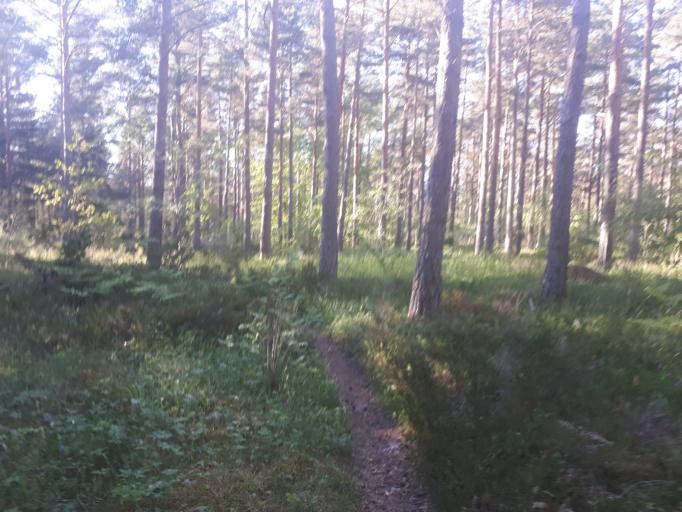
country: SE
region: Gotland
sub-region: Gotland
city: Visby
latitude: 57.6025
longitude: 18.2910
